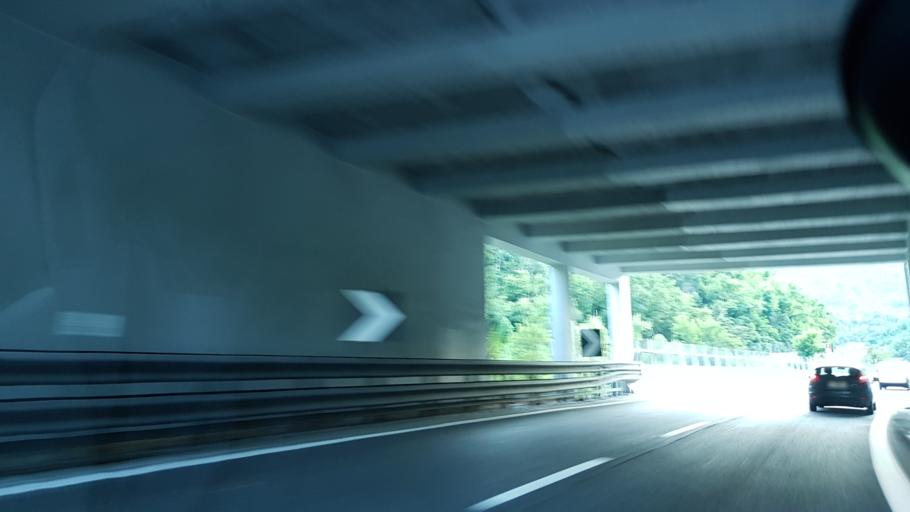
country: IT
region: Liguria
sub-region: Provincia di Genova
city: Isola del Cantone
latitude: 44.6350
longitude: 8.9490
